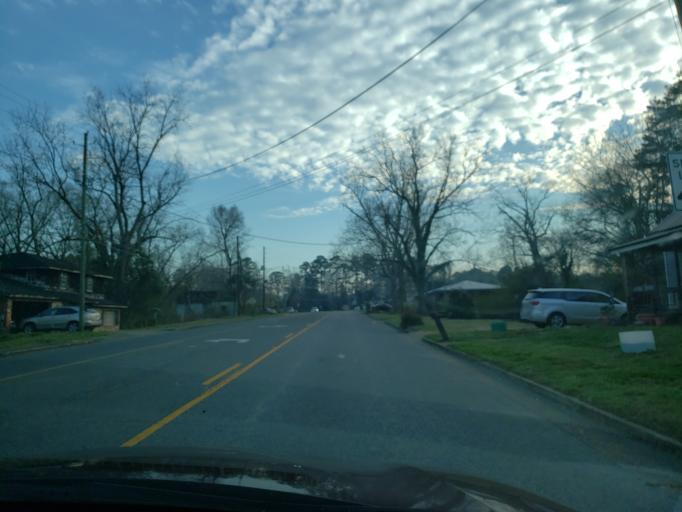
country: US
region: Alabama
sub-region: Hale County
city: Greensboro
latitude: 32.7164
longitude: -87.5951
